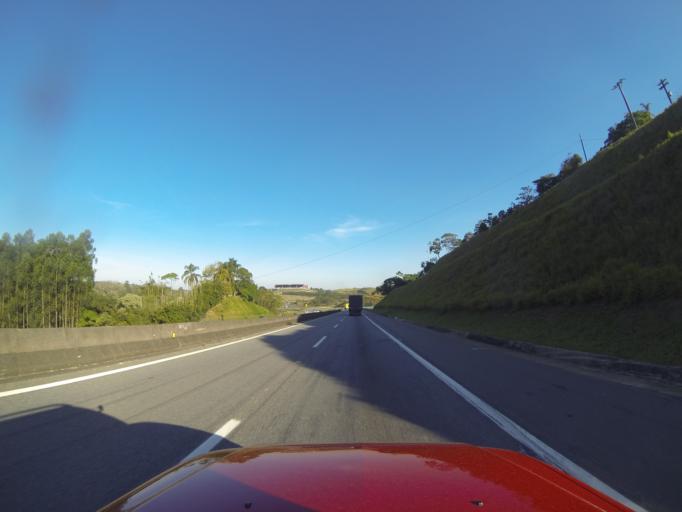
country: BR
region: Sao Paulo
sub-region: Jacarei
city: Jacarei
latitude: -23.2611
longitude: -46.0669
